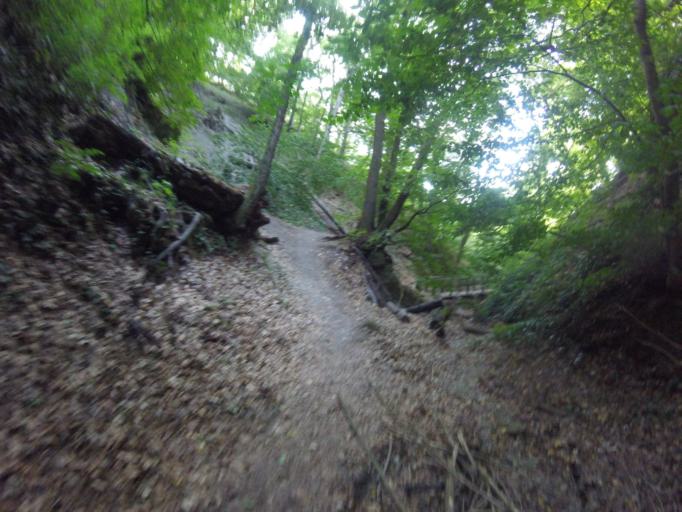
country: HU
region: Pest
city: Csobanka
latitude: 47.6752
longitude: 18.9743
